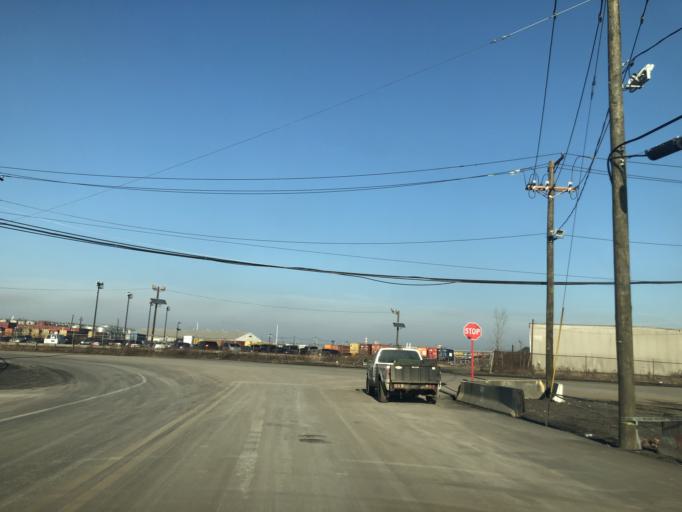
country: US
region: New Jersey
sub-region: Hudson County
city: Bayonne
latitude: 40.6849
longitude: -74.1433
